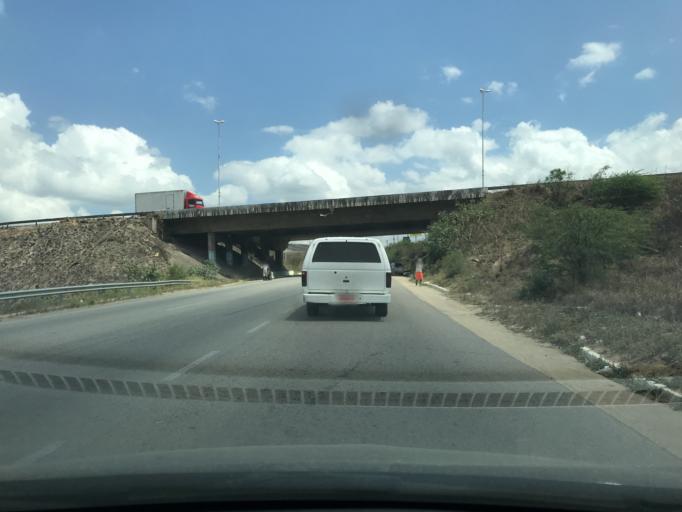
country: BR
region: Pernambuco
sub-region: Caruaru
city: Caruaru
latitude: -8.2994
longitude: -35.9887
